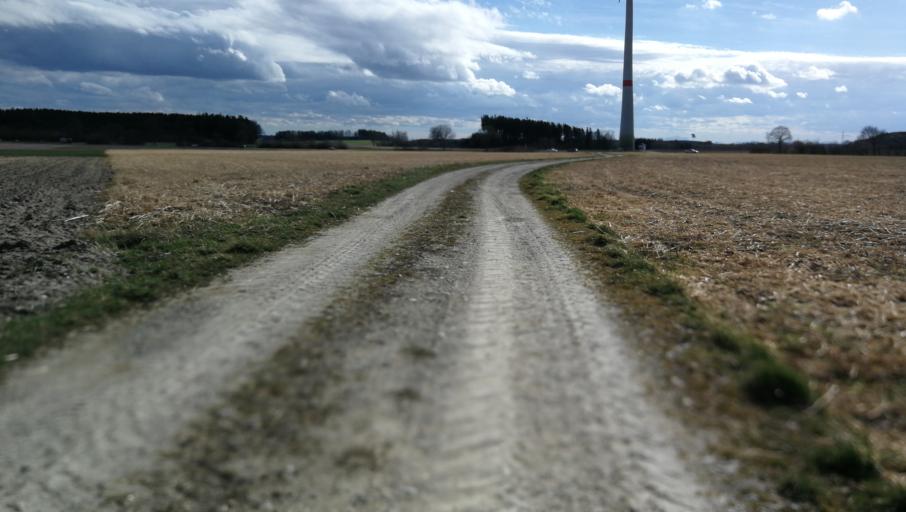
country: DE
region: Bavaria
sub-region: Upper Bavaria
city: Mammendorf
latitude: 48.2023
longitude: 11.1911
